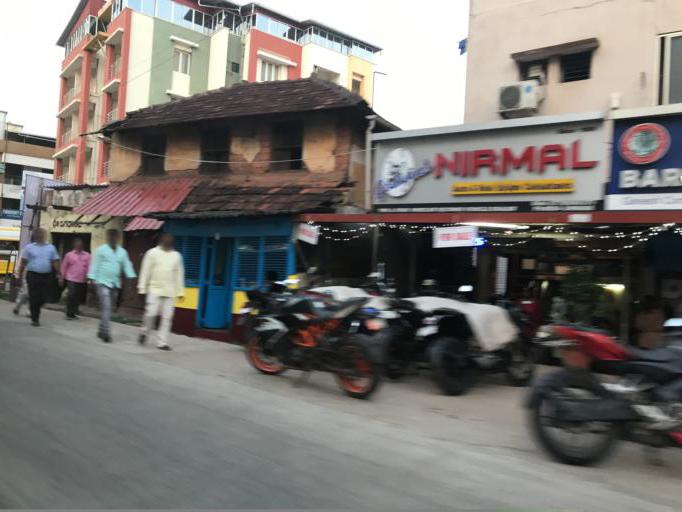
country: IN
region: Karnataka
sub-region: Dakshina Kannada
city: Mangalore
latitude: 12.8772
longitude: 74.8333
